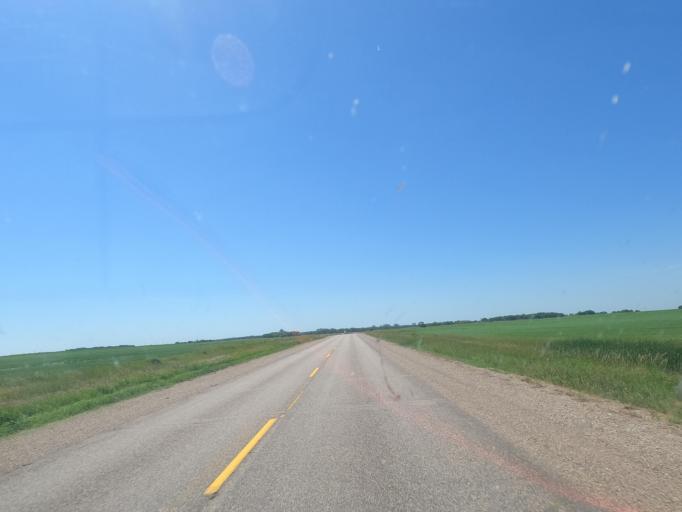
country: CA
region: Manitoba
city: Souris
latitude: 49.6184
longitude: -100.5231
